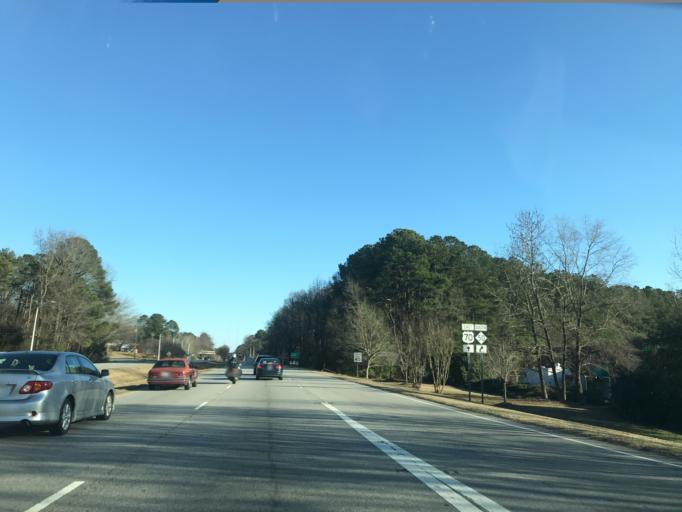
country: US
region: North Carolina
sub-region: Wake County
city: Garner
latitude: 35.7082
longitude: -78.6183
